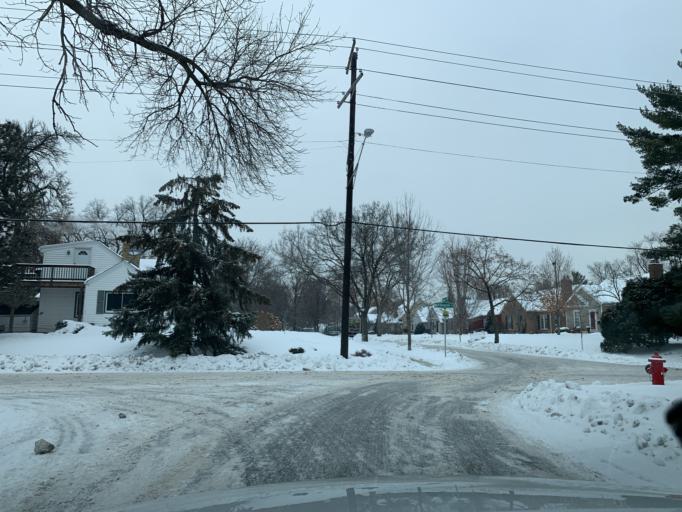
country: US
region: Minnesota
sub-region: Hennepin County
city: Saint Louis Park
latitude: 44.9233
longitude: -93.3472
